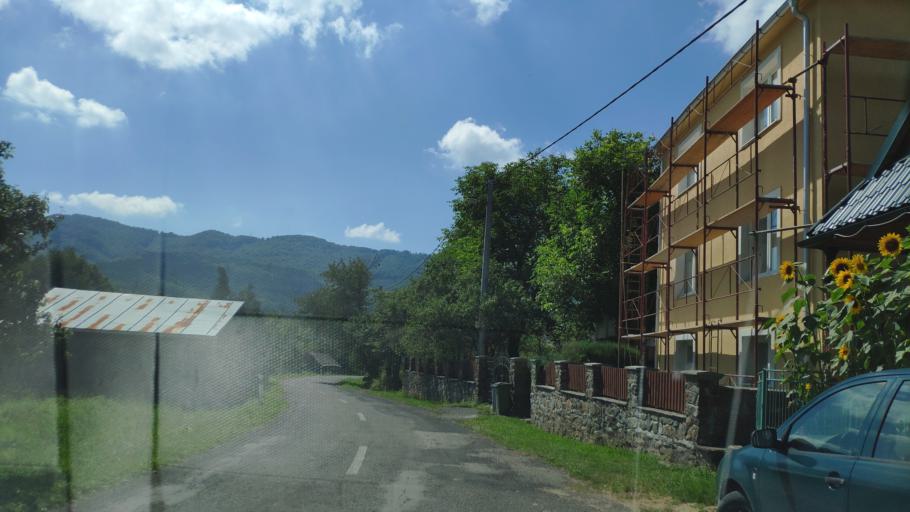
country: PL
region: Subcarpathian Voivodeship
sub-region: Powiat leski
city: Cisna
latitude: 49.0729
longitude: 22.4041
